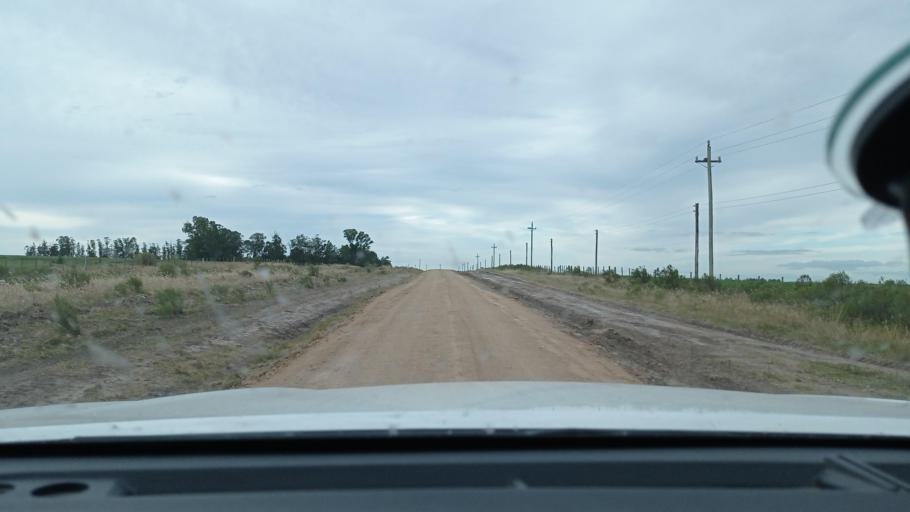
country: UY
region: Florida
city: Casupa
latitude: -34.1141
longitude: -55.7672
